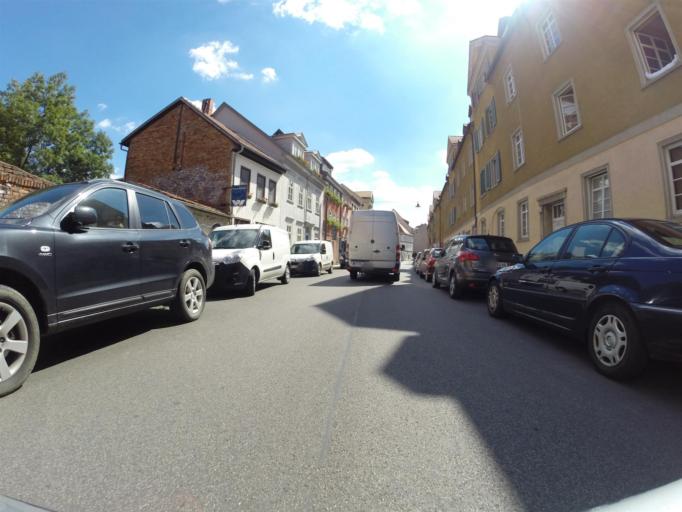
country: DE
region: Thuringia
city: Erfurt
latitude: 50.9816
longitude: 11.0252
